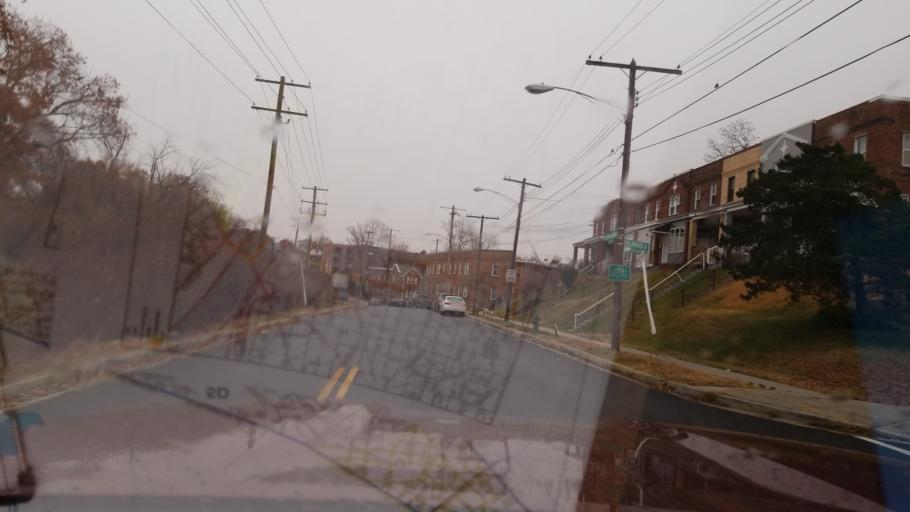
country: US
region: Maryland
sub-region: Prince George's County
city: Silver Hill
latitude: 38.8750
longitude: -76.9694
